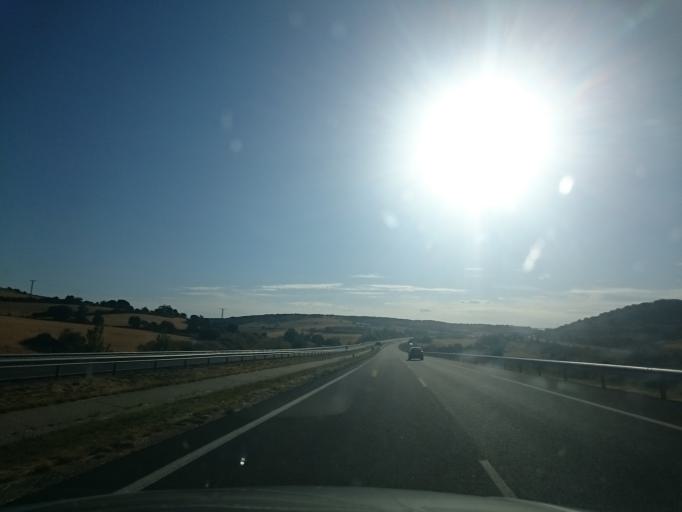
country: ES
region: Castille and Leon
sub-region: Provincia de Burgos
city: Villanueva de Argano
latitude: 42.3802
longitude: -3.9452
